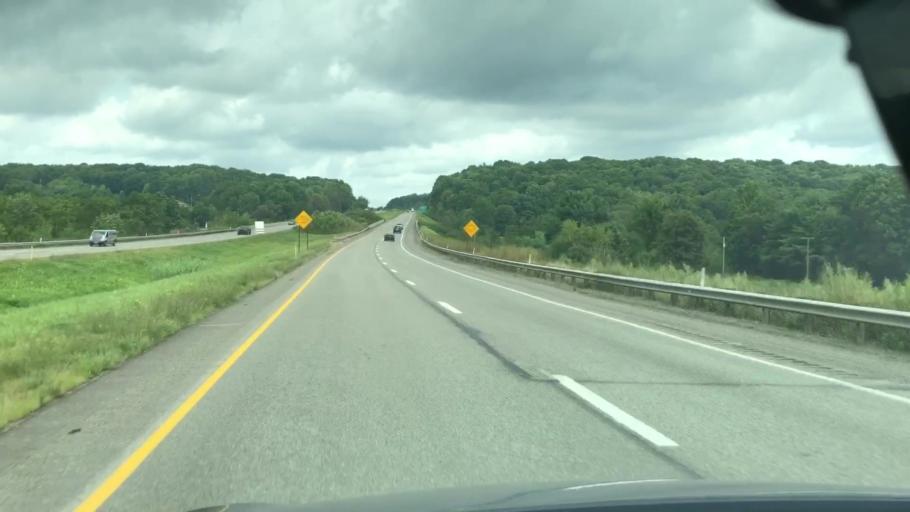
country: US
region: Pennsylvania
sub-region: Crawford County
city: Meadville
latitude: 41.5897
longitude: -80.1726
